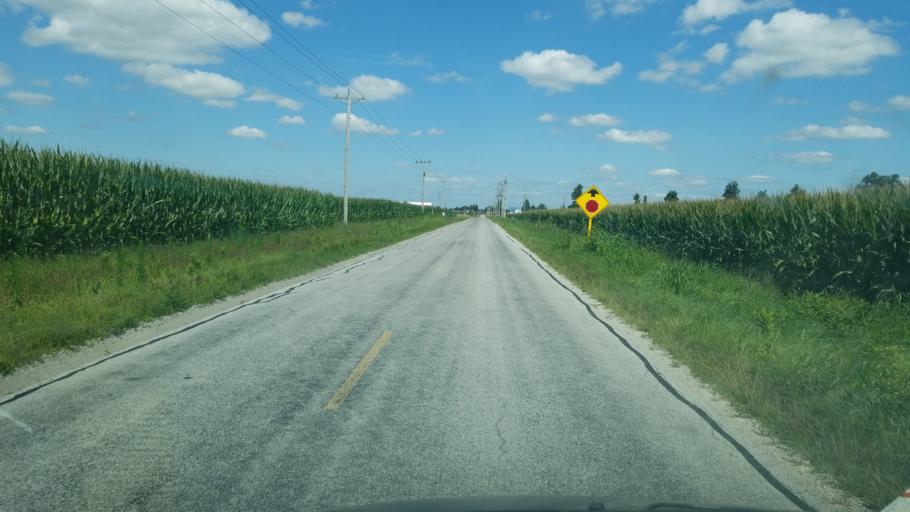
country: US
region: Ohio
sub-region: Fulton County
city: Swanton
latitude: 41.5711
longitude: -83.9408
